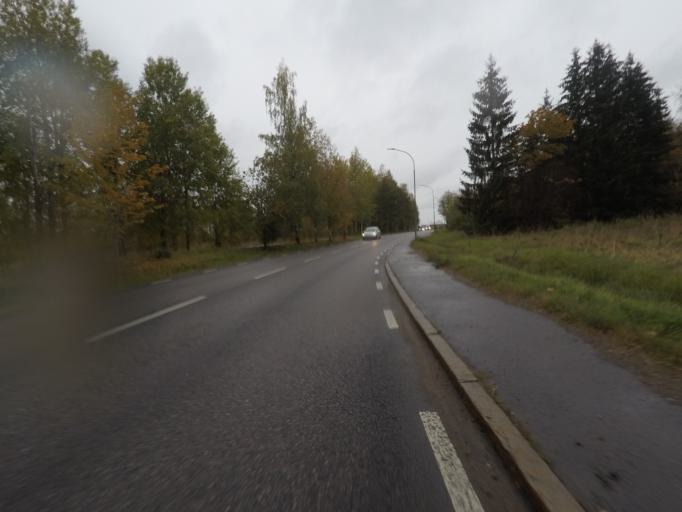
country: SE
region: OErebro
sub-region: Karlskoga Kommun
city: Karlskoga
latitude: 59.3220
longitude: 14.4776
